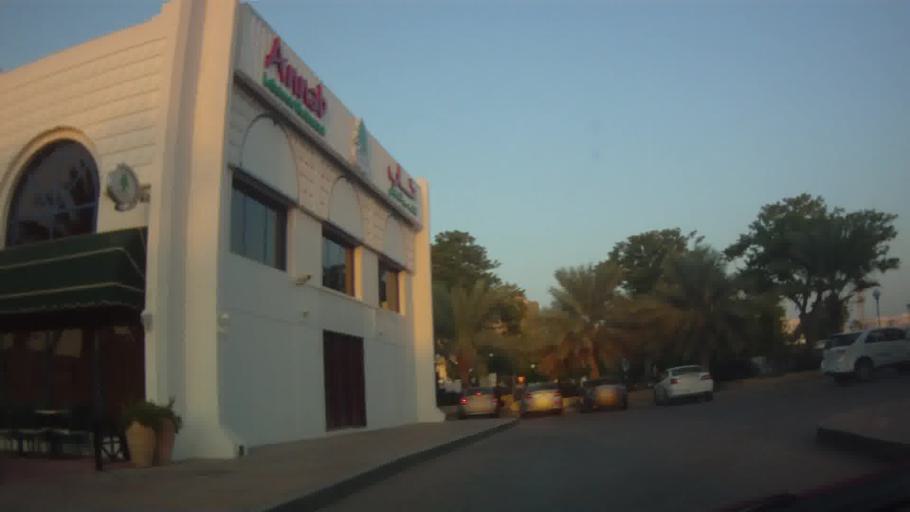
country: OM
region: Muhafazat Masqat
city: Bawshar
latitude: 23.6156
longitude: 58.4628
